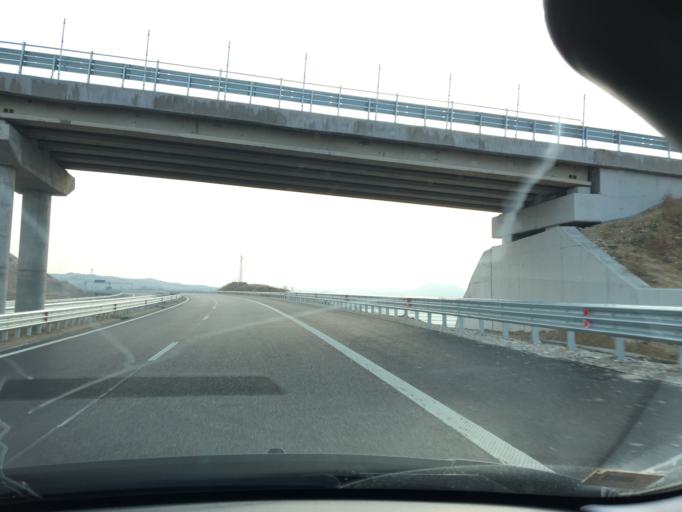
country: BG
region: Blagoevgrad
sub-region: Obshtina Sandanski
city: Sandanski
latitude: 41.5316
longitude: 23.2595
